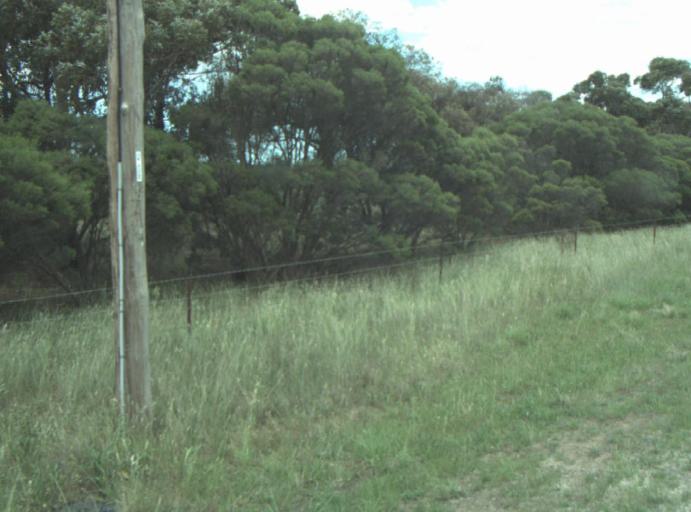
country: AU
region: Victoria
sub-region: Wyndham
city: Little River
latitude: -37.9263
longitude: 144.4644
